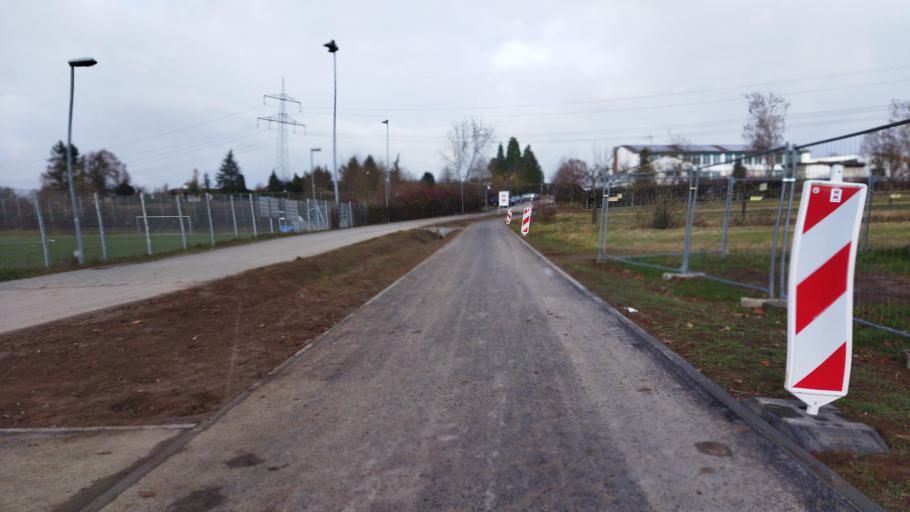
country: DE
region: Baden-Wuerttemberg
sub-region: Regierungsbezirk Stuttgart
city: Erligheim
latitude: 49.0213
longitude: 9.1043
